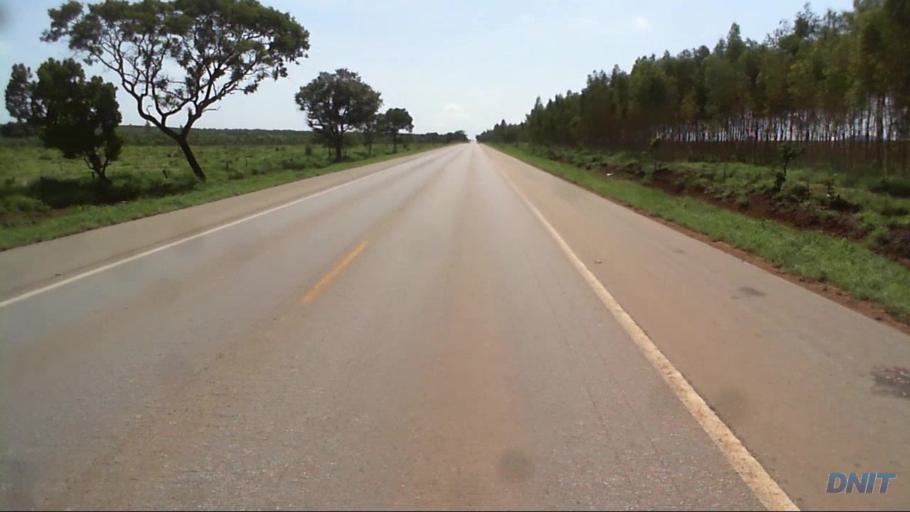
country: BR
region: Goias
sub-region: Barro Alto
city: Barro Alto
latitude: -15.2043
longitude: -48.7358
